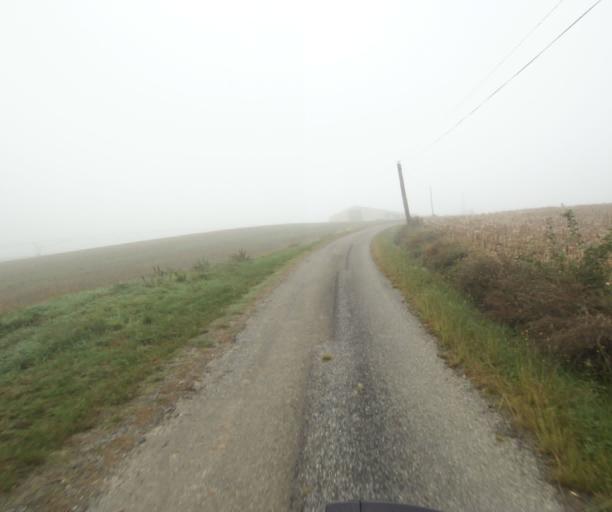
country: FR
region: Midi-Pyrenees
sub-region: Departement du Tarn-et-Garonne
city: Nohic
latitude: 43.9062
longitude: 1.4753
